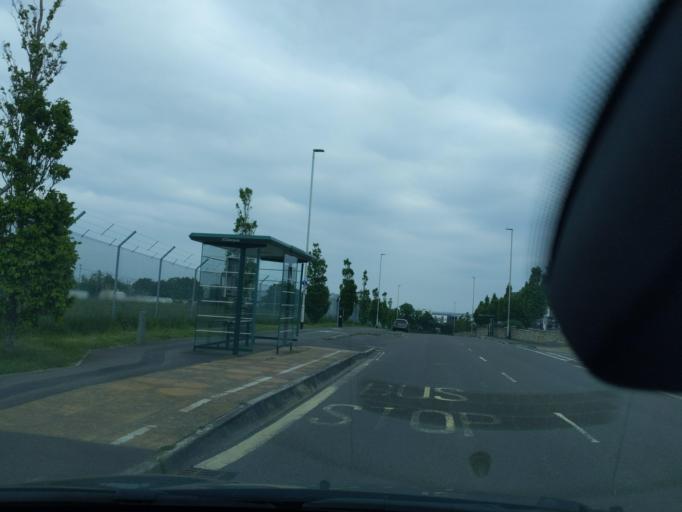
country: GB
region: England
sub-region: Plymouth
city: Plymouth
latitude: 50.4222
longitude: -4.1139
